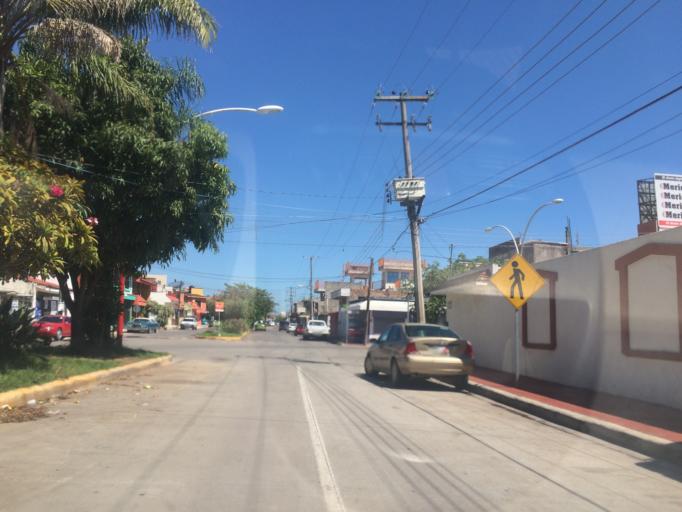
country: MX
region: Nayarit
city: Tepic
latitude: 21.4938
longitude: -104.8799
